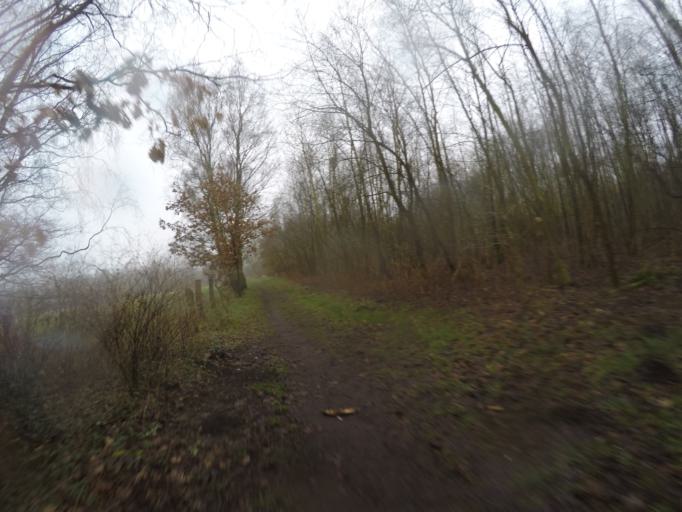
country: DE
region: Schleswig-Holstein
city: Quickborn
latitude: 53.7195
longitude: 9.9317
